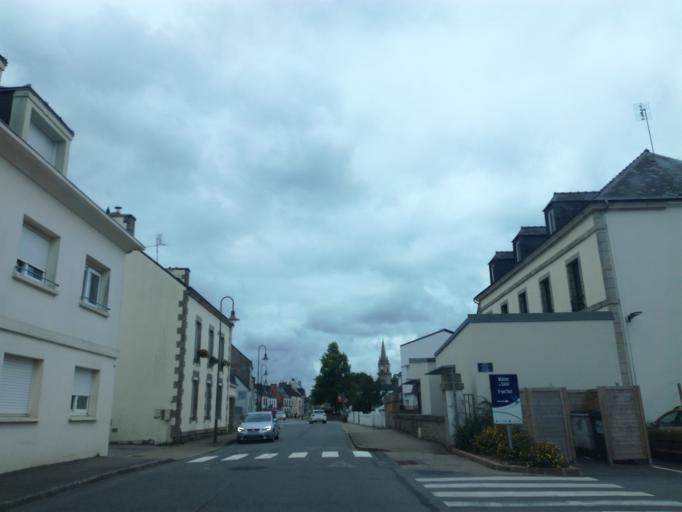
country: FR
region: Brittany
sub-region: Departement du Morbihan
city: Cleguerec
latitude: 48.1261
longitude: -3.0719
